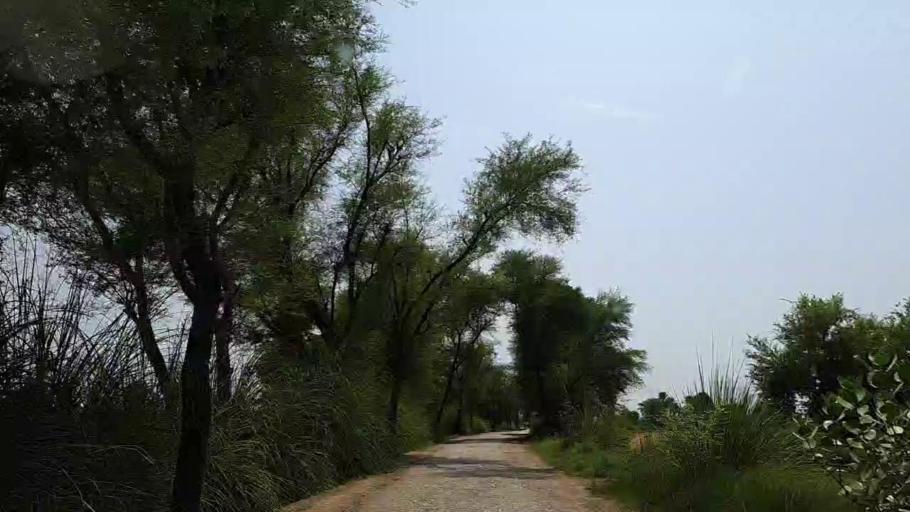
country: PK
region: Sindh
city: Adilpur
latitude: 27.9261
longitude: 69.3782
